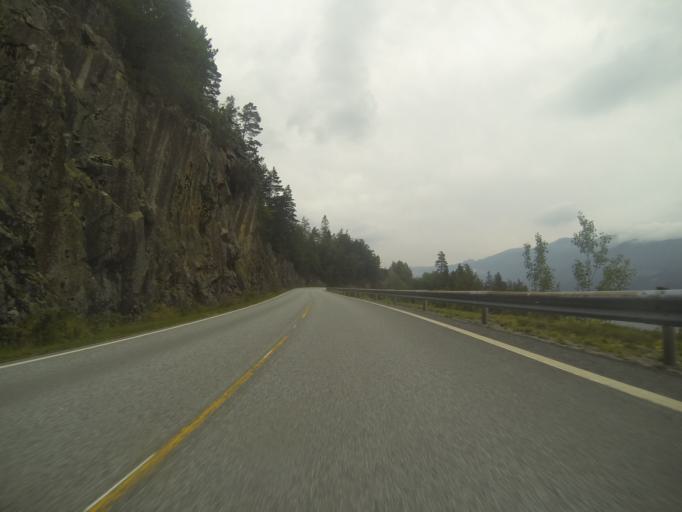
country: NO
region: Rogaland
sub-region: Suldal
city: Sand
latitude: 59.5590
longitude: 6.2656
